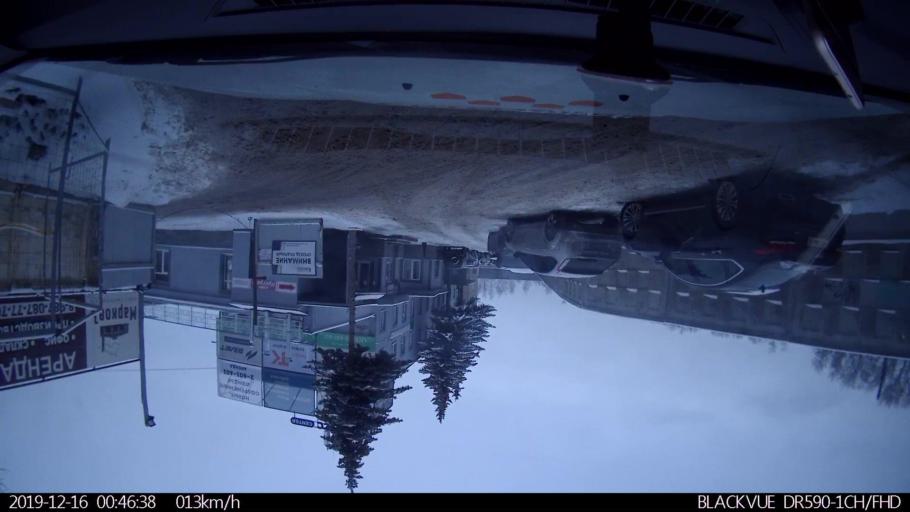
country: RU
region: Nizjnij Novgorod
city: Gorbatovka
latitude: 56.3110
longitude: 43.8576
